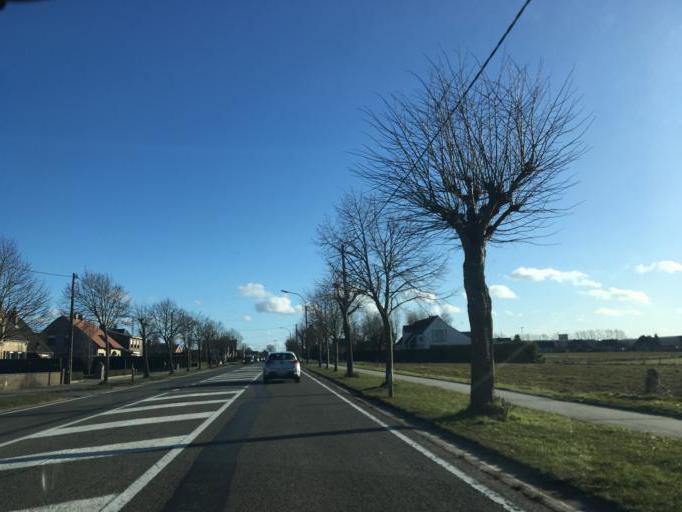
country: BE
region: Flanders
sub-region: Provincie West-Vlaanderen
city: Hooglede
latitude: 51.0011
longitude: 3.1159
